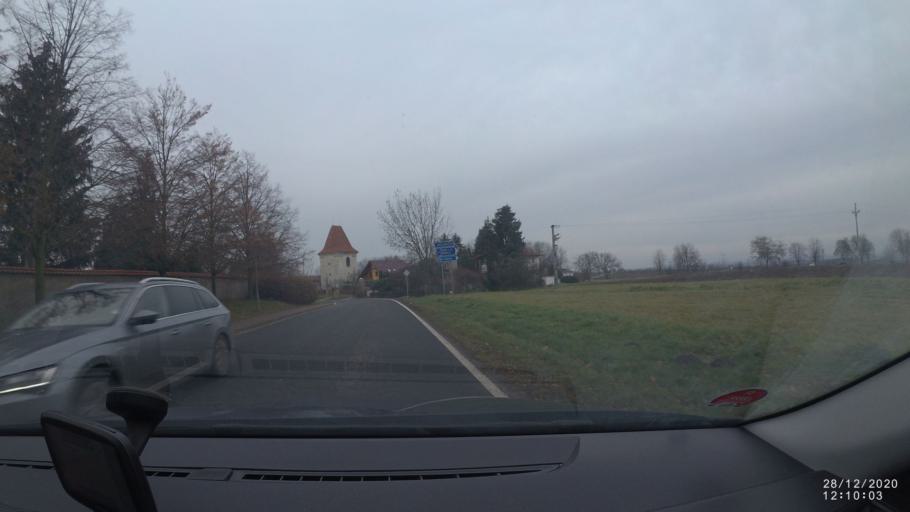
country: CZ
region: Central Bohemia
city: Brandys nad Labem-Stara Boleslav
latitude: 50.1683
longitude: 14.6335
